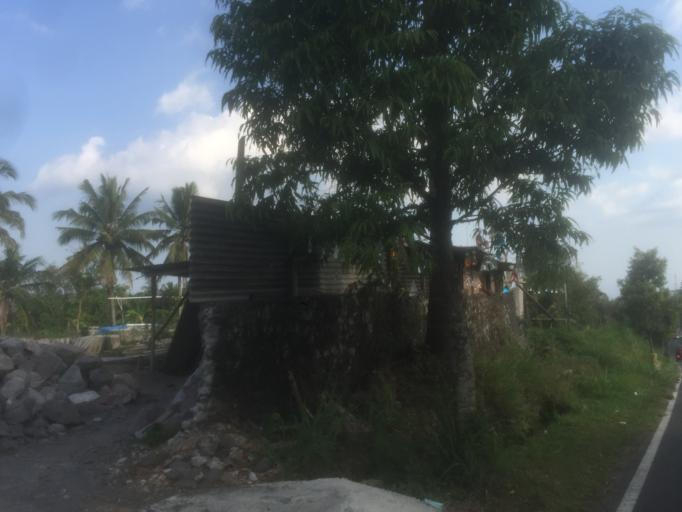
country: ID
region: Daerah Istimewa Yogyakarta
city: Sleman
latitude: -7.6426
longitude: 110.4250
